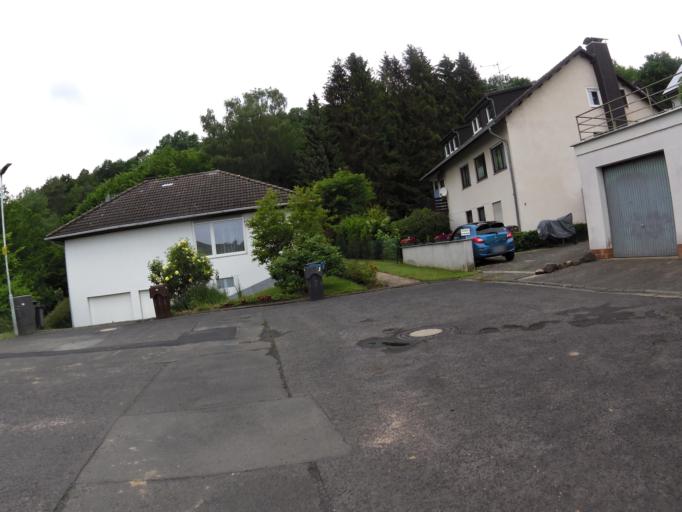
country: DE
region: Hesse
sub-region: Regierungsbezirk Kassel
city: Bad Hersfeld
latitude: 50.8724
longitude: 9.6768
